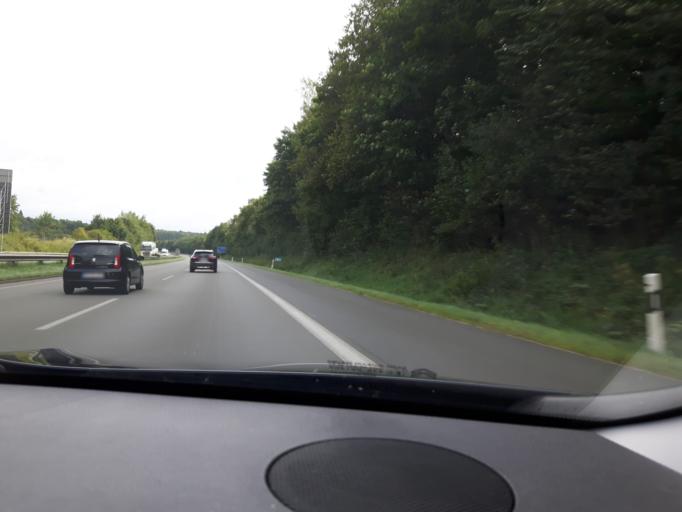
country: DE
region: Lower Saxony
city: Seevetal
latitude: 53.4044
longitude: 9.9100
